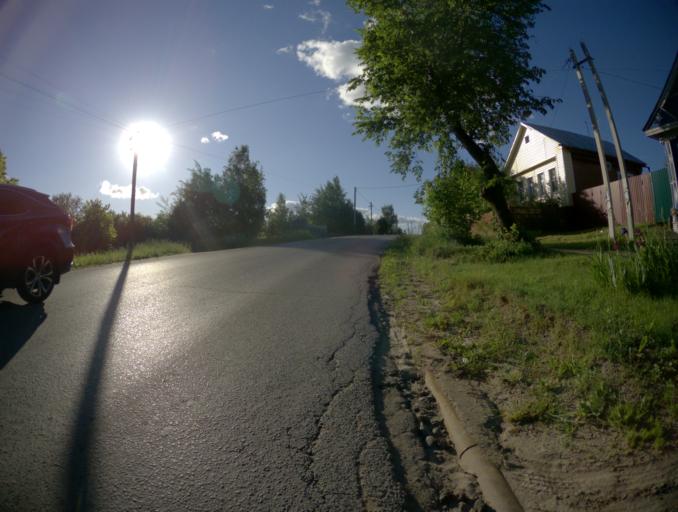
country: RU
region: Ivanovo
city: Lezhnevo
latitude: 56.7786
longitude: 40.8919
